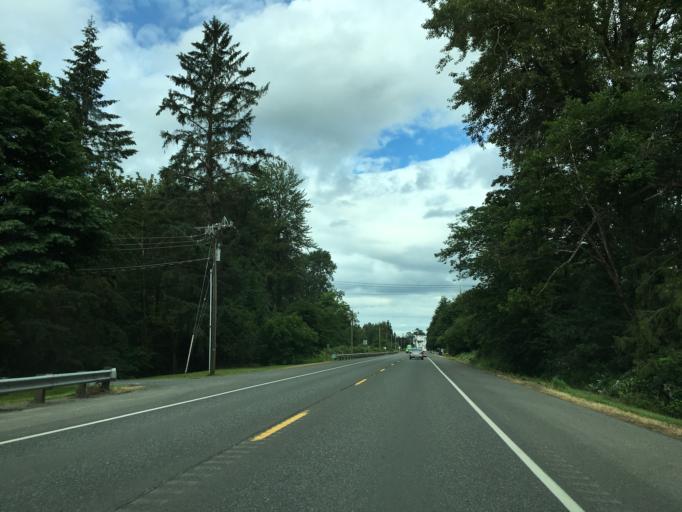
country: US
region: Washington
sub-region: Whatcom County
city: Peaceful Valley
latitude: 48.8295
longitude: -122.2279
